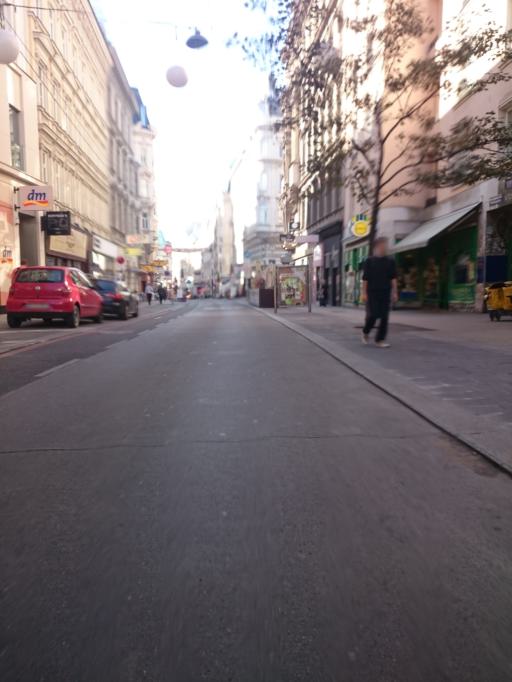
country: AT
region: Vienna
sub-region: Wien Stadt
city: Vienna
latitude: 48.2004
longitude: 16.3492
